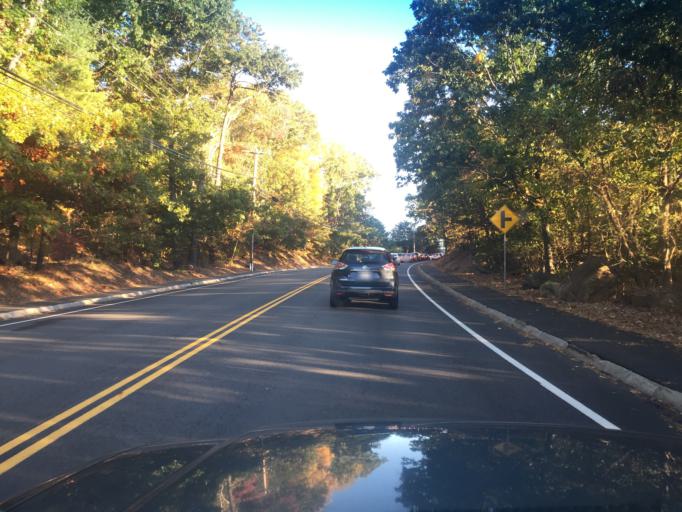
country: US
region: Massachusetts
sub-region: Middlesex County
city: Marlborough
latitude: 42.3640
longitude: -71.5546
